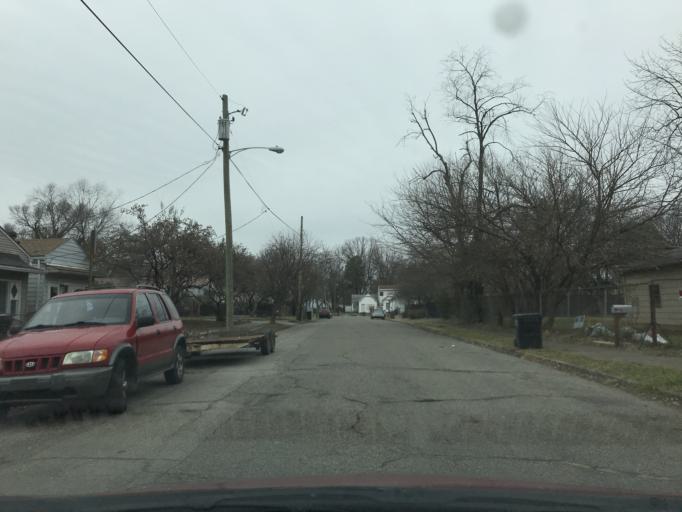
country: US
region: Kentucky
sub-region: Jefferson County
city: Louisville
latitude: 38.2687
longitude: -85.7861
